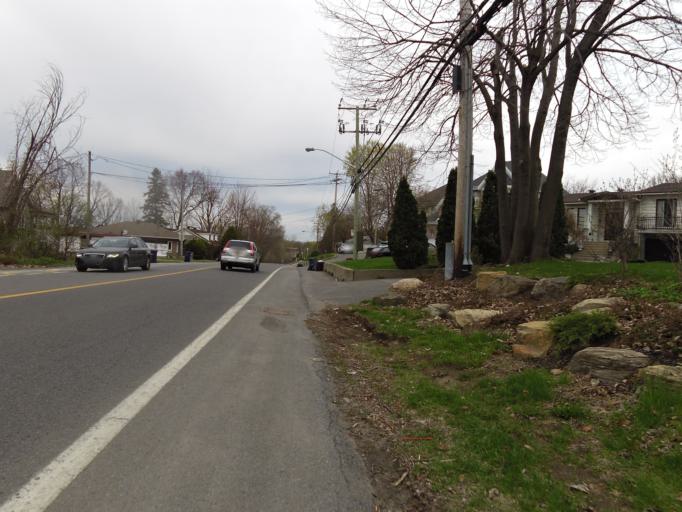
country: CA
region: Quebec
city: Dollard-Des Ormeaux
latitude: 45.5208
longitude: -73.8265
